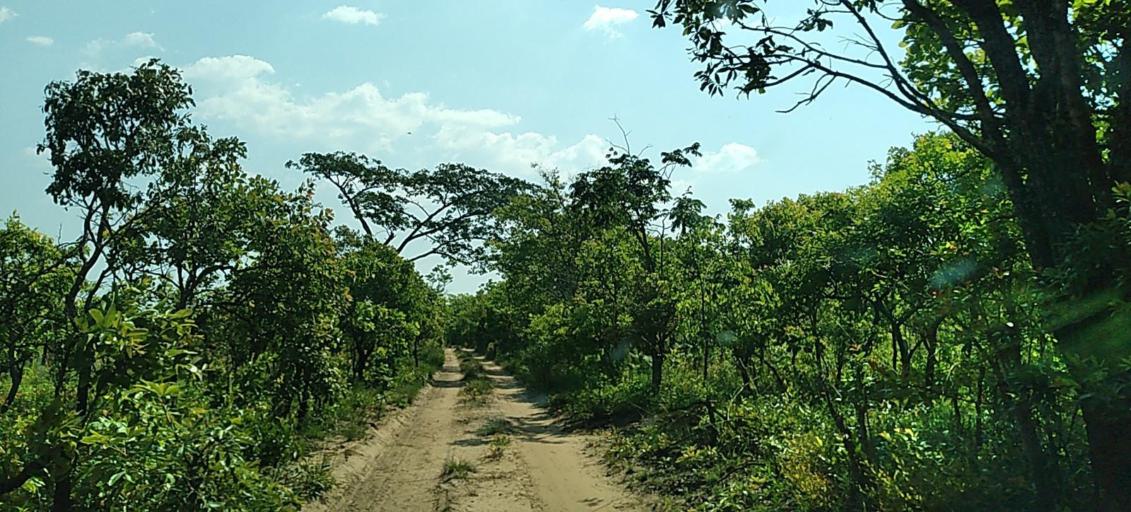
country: CD
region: Katanga
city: Kolwezi
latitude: -11.2655
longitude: 25.0005
